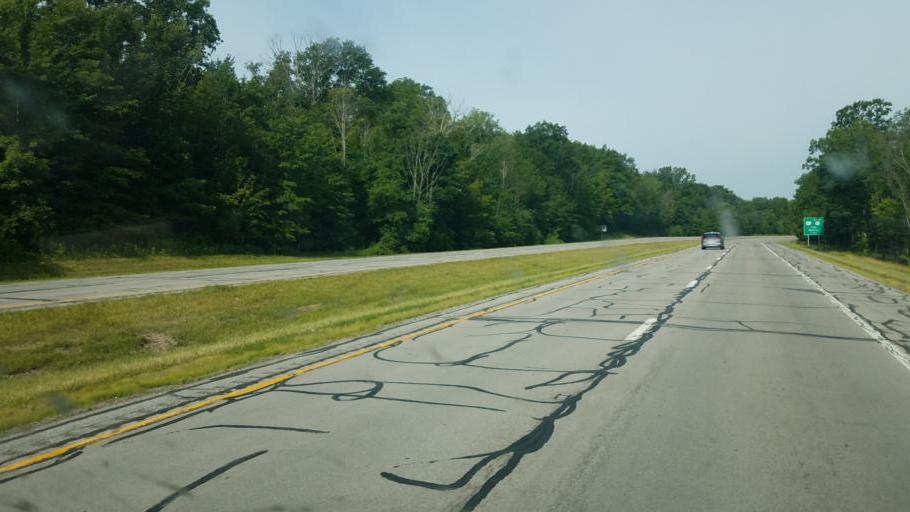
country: US
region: Ohio
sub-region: Medina County
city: Lodi
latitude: 41.0385
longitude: -81.9733
